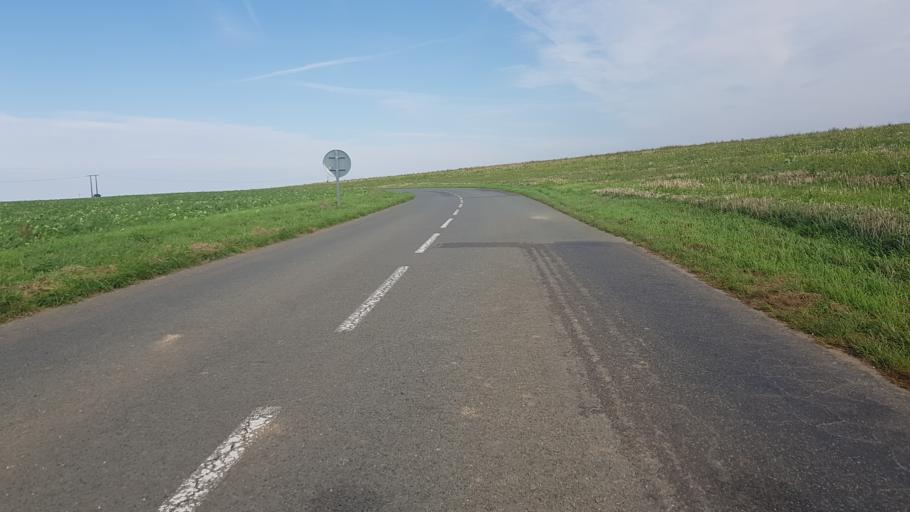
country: FR
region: Poitou-Charentes
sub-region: Departement de la Vienne
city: Chasseneuil-du-Poitou
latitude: 46.6478
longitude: 0.3492
